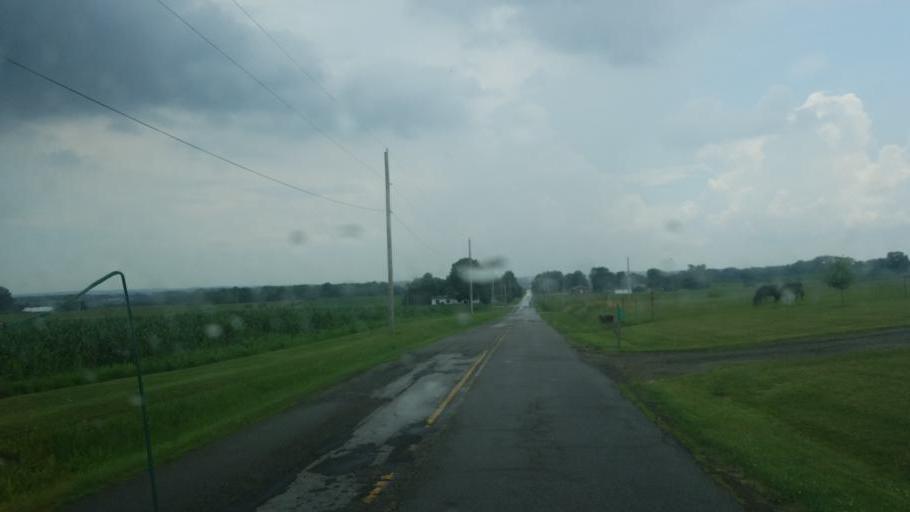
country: US
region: Ohio
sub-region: Wayne County
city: Smithville
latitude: 40.9017
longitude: -81.8435
